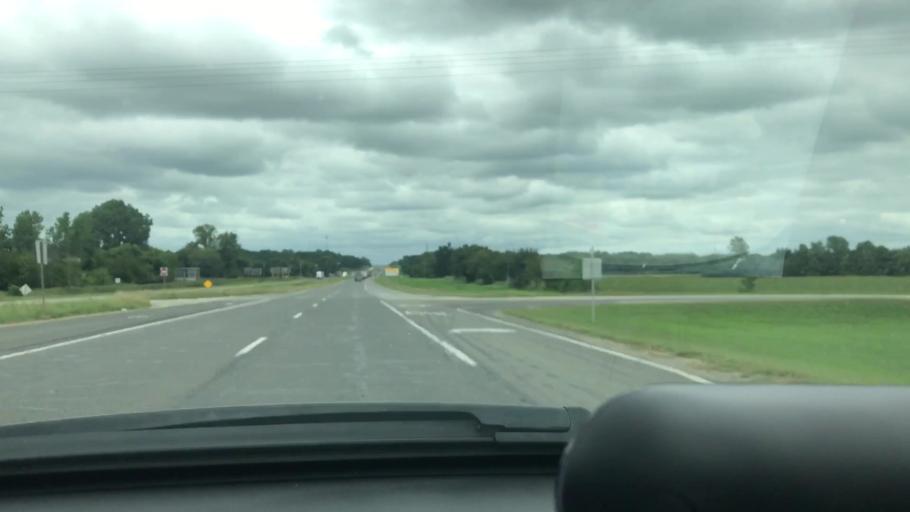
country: US
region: Oklahoma
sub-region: Muskogee County
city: Muskogee
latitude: 35.8126
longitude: -95.4023
